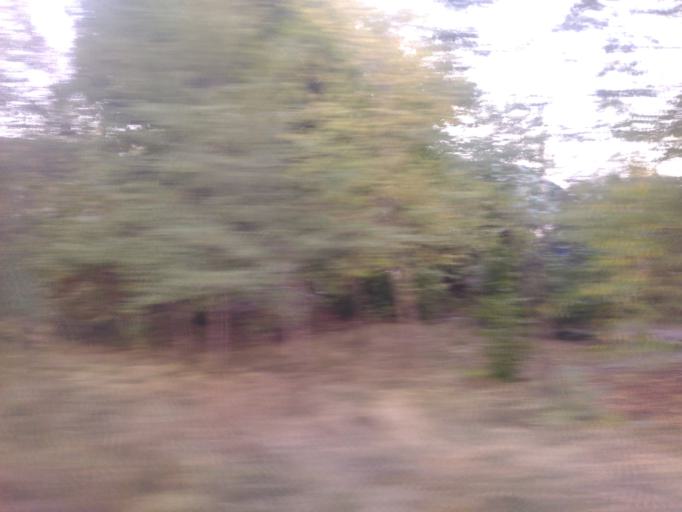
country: RU
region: Ulyanovsk
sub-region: Ulyanovskiy Rayon
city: Ulyanovsk
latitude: 54.2631
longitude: 48.2810
